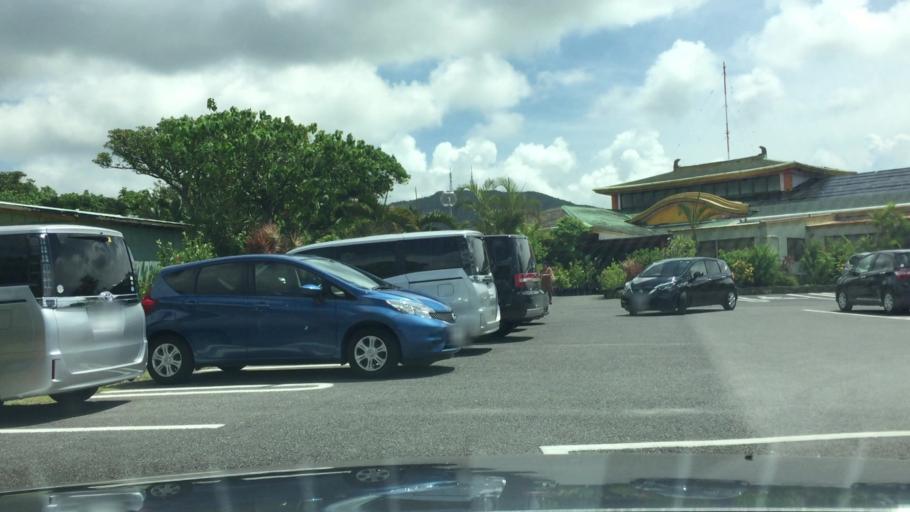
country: JP
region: Okinawa
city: Ishigaki
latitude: 24.3616
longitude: 124.1538
